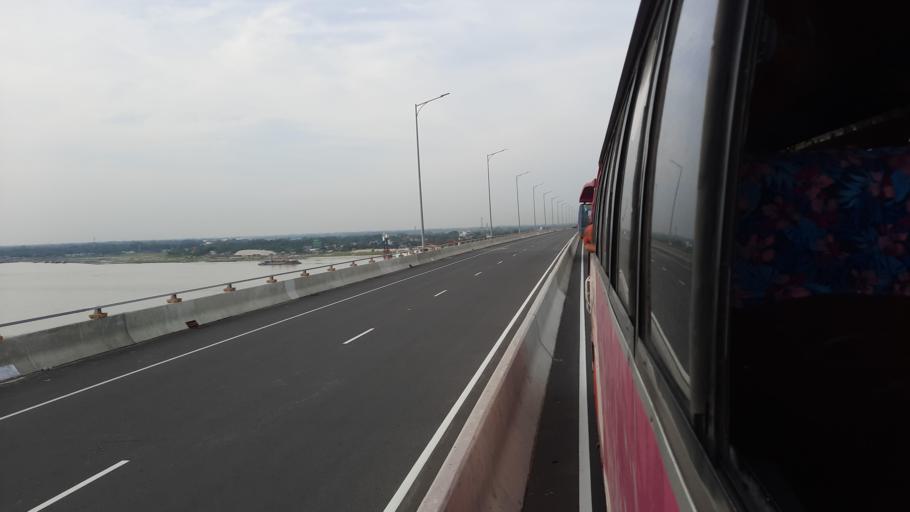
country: BD
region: Dhaka
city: Char Bhadrasan
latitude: 23.4628
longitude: 90.2630
